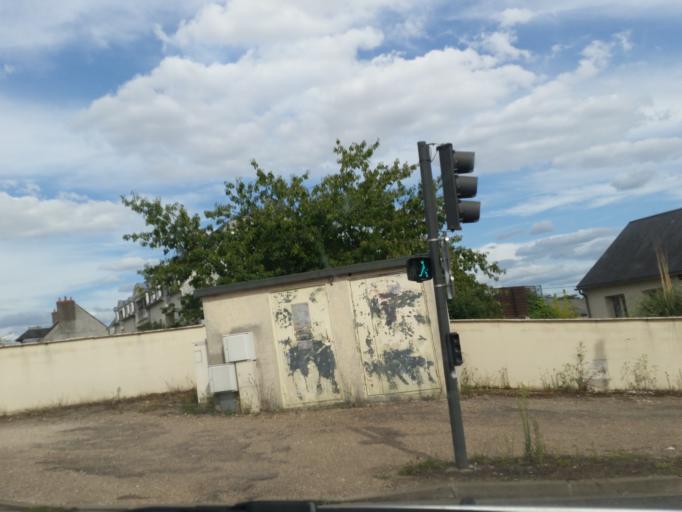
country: FR
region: Centre
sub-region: Departement du Loir-et-Cher
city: Blois
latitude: 47.5871
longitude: 1.3464
